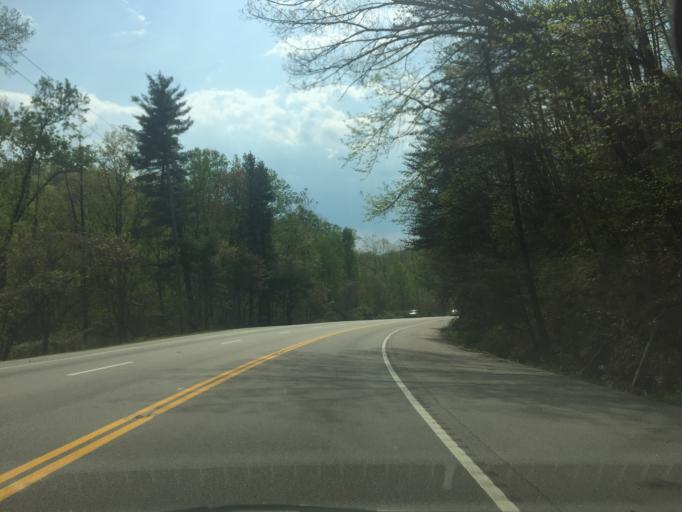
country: US
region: Tennessee
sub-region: Hamilton County
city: Signal Mountain
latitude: 35.1204
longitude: -85.3473
